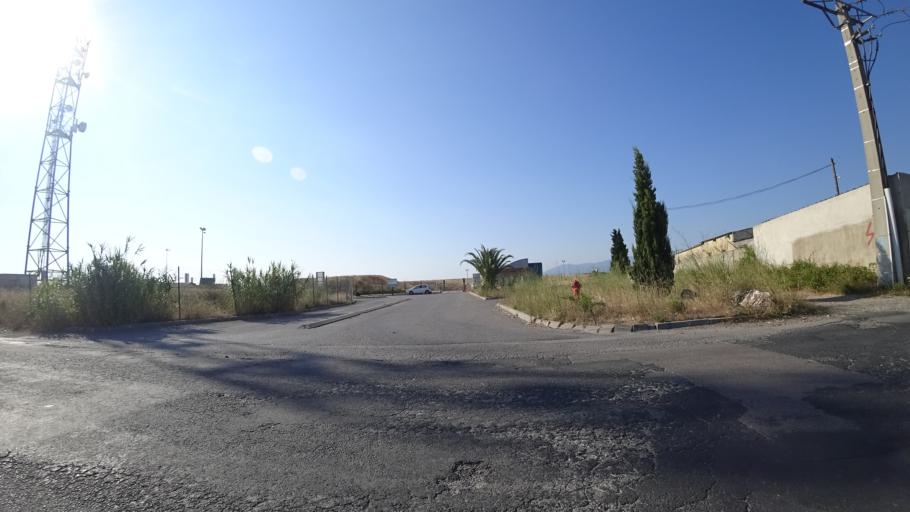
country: FR
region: Languedoc-Roussillon
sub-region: Departement des Pyrenees-Orientales
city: Cabestany
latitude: 42.6885
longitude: 2.9688
